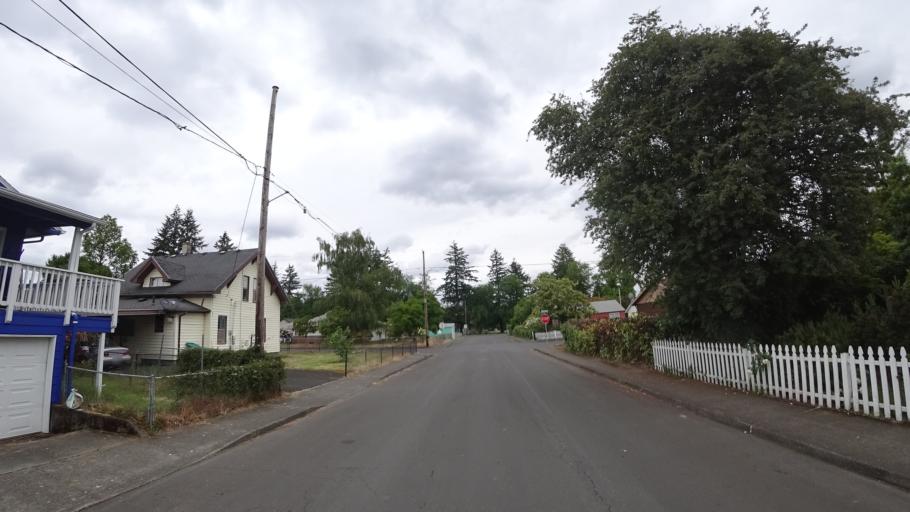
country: US
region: Oregon
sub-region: Multnomah County
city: Lents
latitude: 45.4880
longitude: -122.5738
